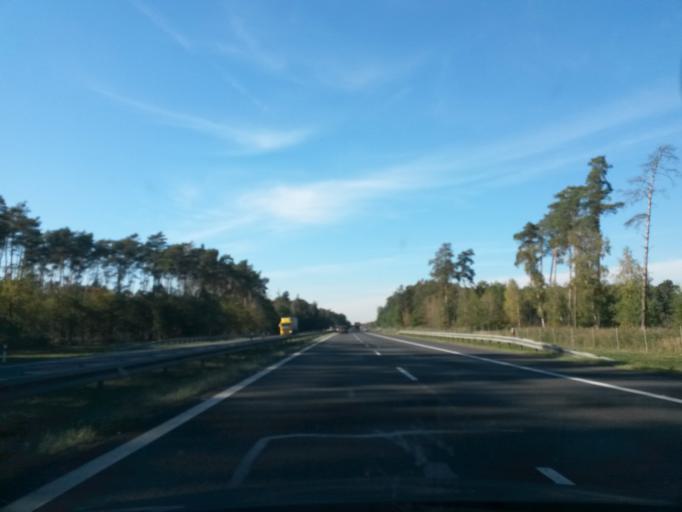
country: PL
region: Opole Voivodeship
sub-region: Powiat opolski
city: Niemodlin
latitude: 50.6935
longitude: 17.6275
